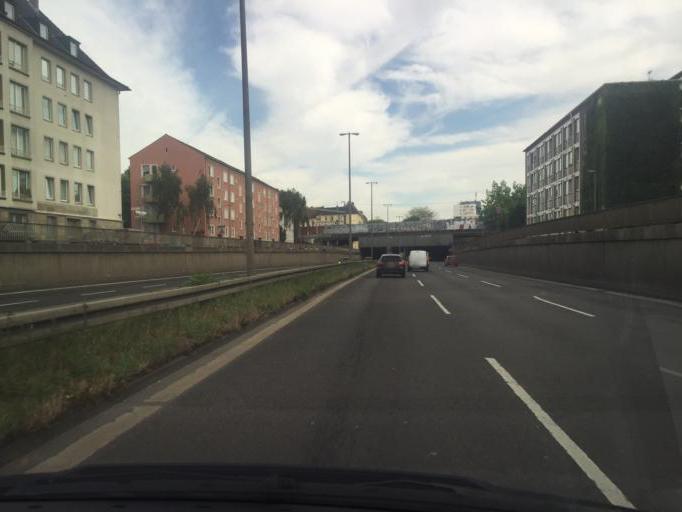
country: DE
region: North Rhine-Westphalia
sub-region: Regierungsbezirk Koln
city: Neuehrenfeld
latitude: 50.9517
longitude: 6.9338
